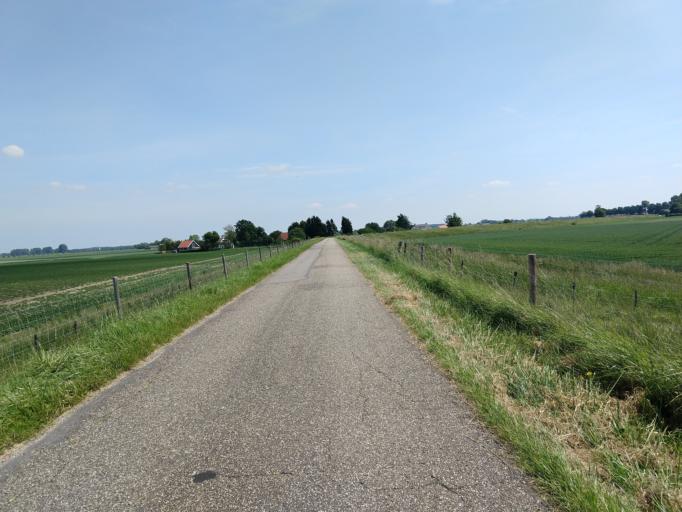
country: NL
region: Zeeland
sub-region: Gemeente Borsele
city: Borssele
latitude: 51.4728
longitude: 3.7583
